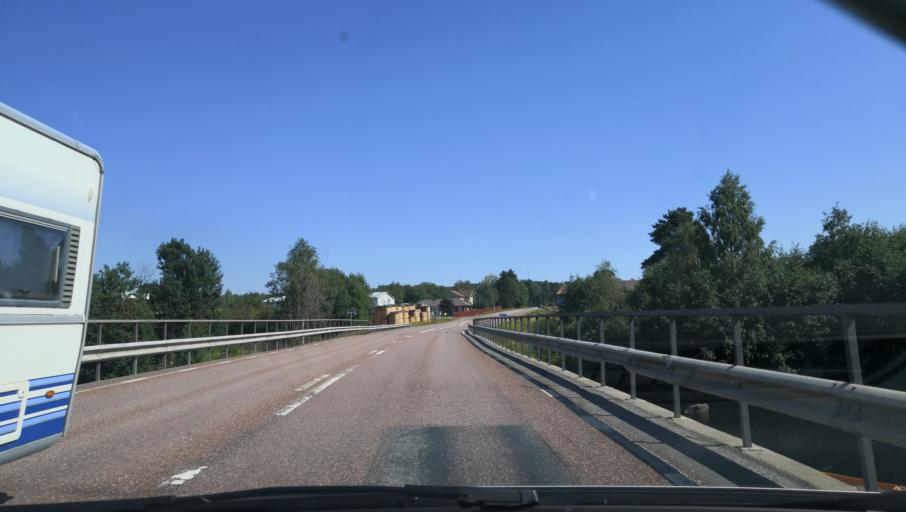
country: SE
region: Gaevleborg
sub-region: Ovanakers Kommun
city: Edsbyn
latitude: 61.3640
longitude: 15.9161
